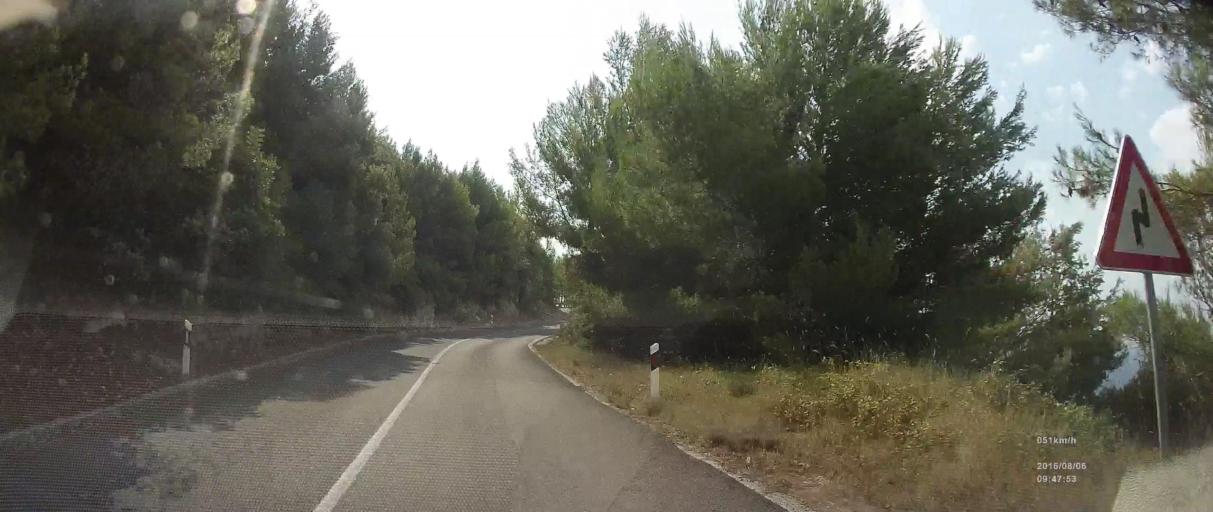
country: HR
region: Dubrovacko-Neretvanska
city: Blato
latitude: 42.7384
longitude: 17.5306
